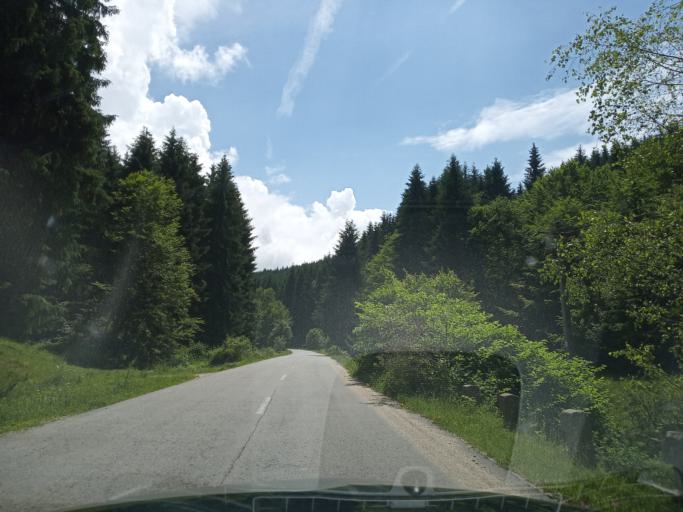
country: RO
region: Hunedoara
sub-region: Oras Petrila
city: Petrila
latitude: 45.3972
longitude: 23.4197
